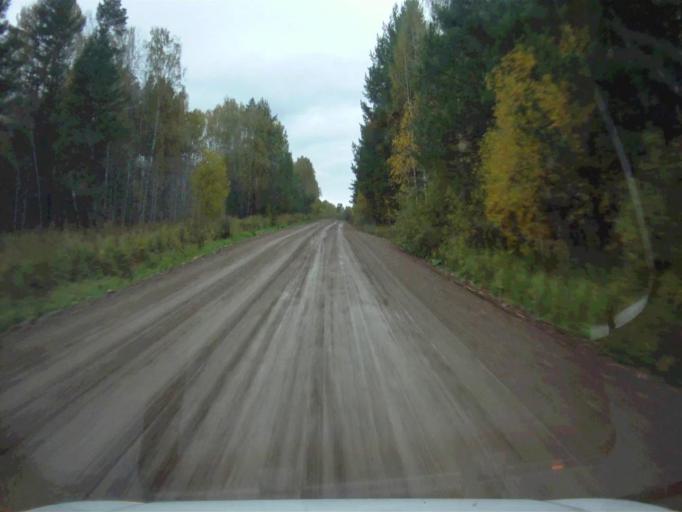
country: RU
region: Chelyabinsk
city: Nyazepetrovsk
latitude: 56.0975
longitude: 59.3960
